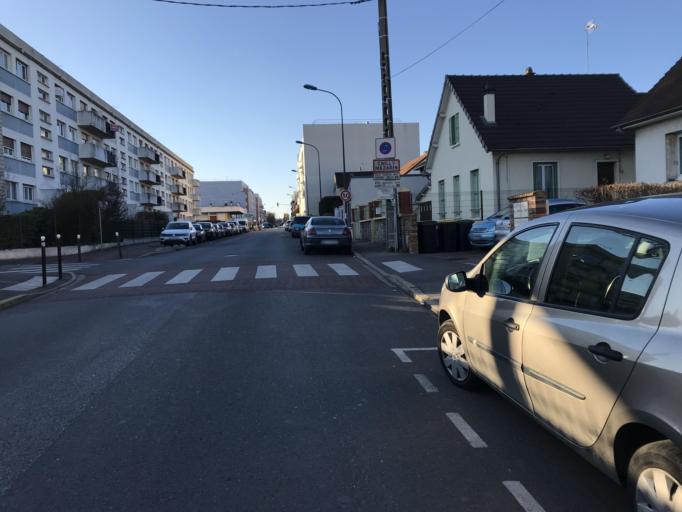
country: FR
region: Ile-de-France
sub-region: Departement de l'Essonne
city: Chilly-Mazarin
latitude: 48.7015
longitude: 2.3227
